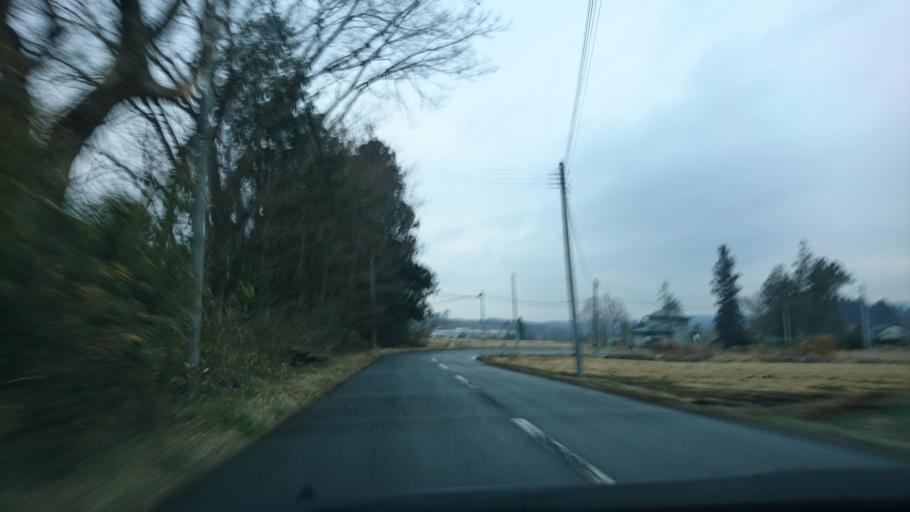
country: JP
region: Iwate
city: Ichinoseki
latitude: 39.0170
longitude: 141.3511
